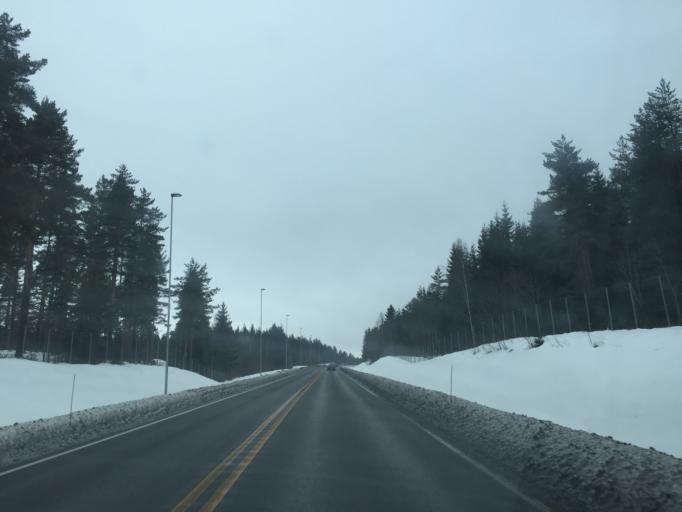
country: NO
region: Hedmark
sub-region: Loten
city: Loten
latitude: 60.7459
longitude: 11.3003
